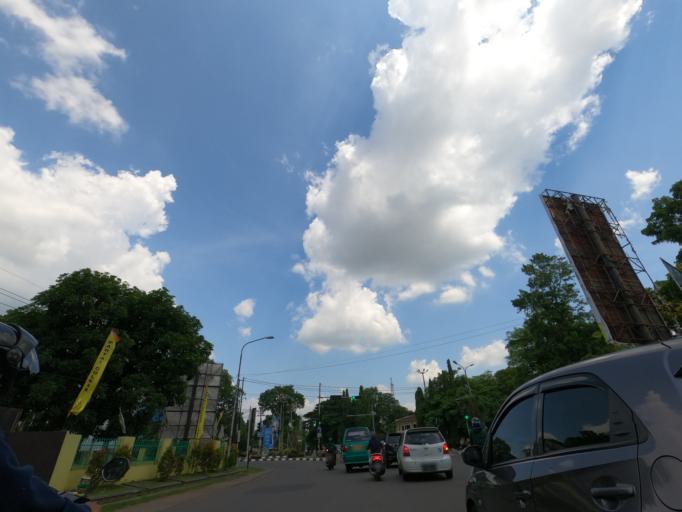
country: ID
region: West Java
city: Pamanukan
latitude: -6.5559
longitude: 107.7608
